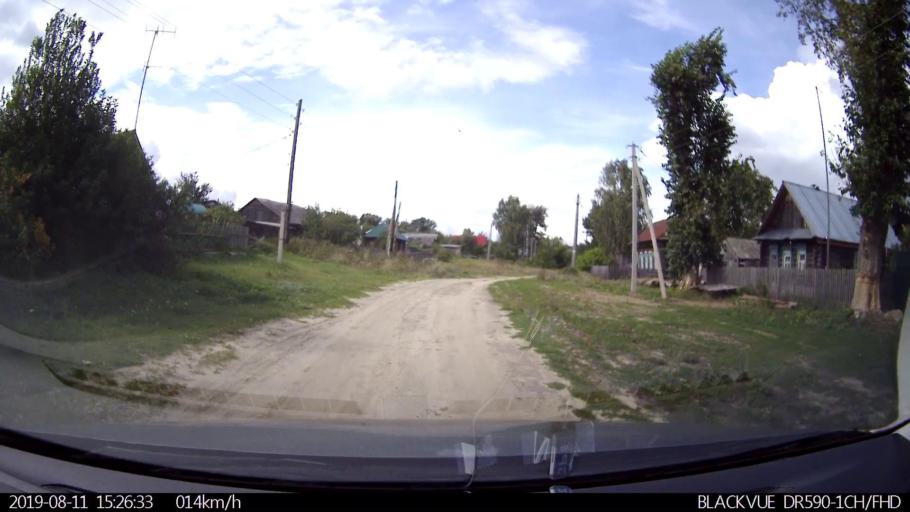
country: RU
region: Ulyanovsk
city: Ignatovka
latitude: 53.8504
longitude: 47.5758
